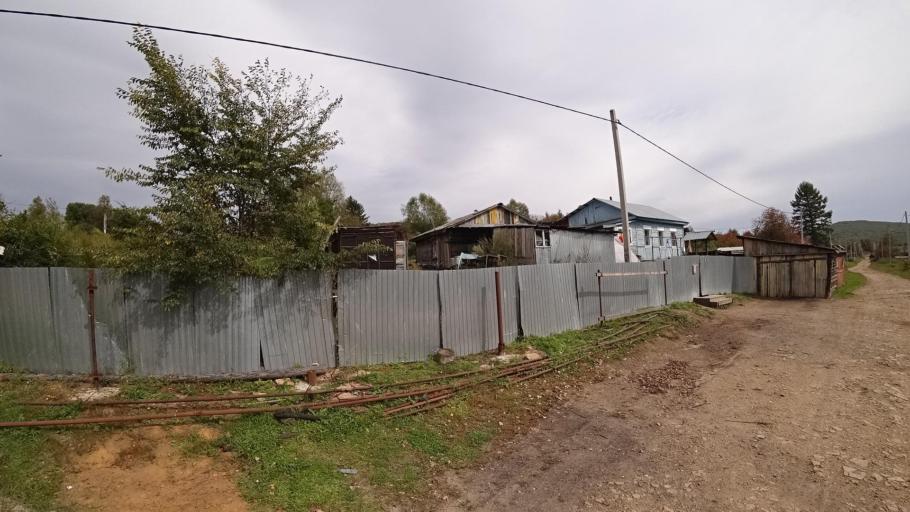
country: RU
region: Jewish Autonomous Oblast
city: Khingansk
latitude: 49.1260
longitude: 131.2037
